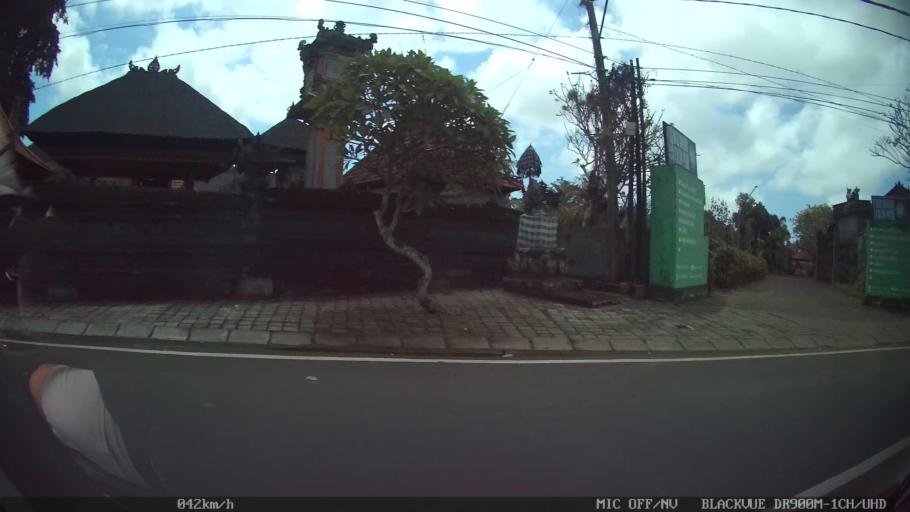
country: ID
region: Bali
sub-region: Kabupaten Gianyar
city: Ubud
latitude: -8.5468
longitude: 115.2812
